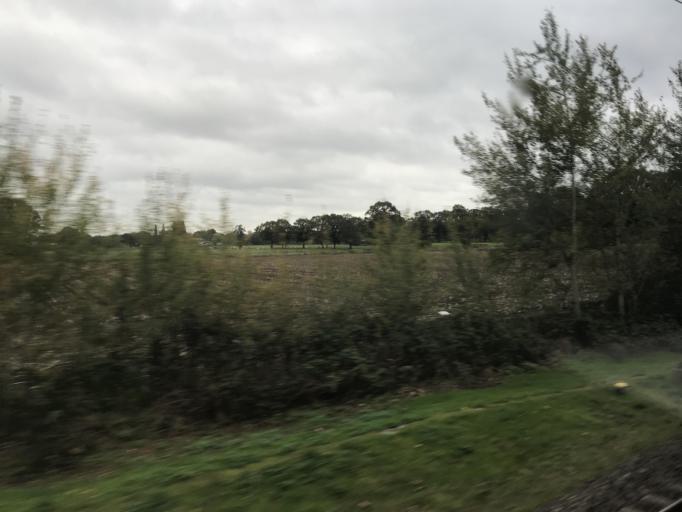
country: DE
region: Lower Saxony
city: Leer
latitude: 53.1562
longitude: 7.4417
